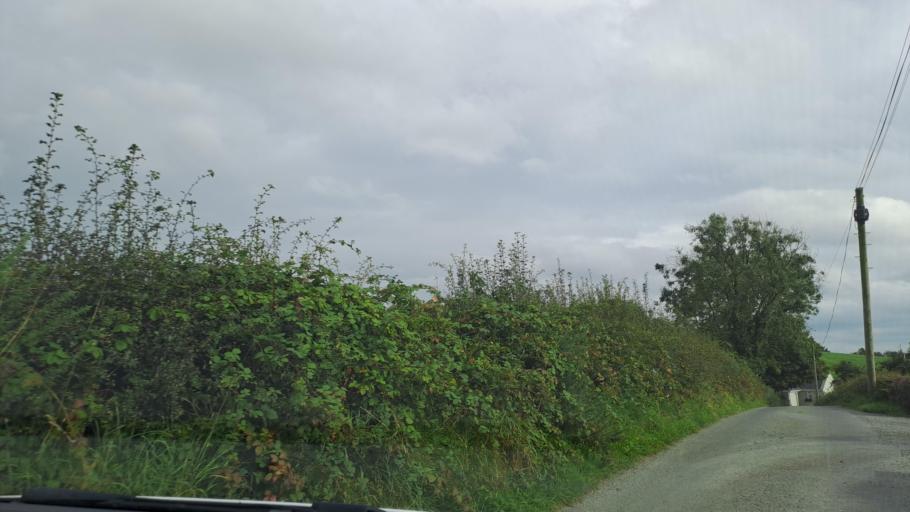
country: IE
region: Ulster
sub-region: An Cabhan
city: Kingscourt
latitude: 53.9801
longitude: -6.8581
